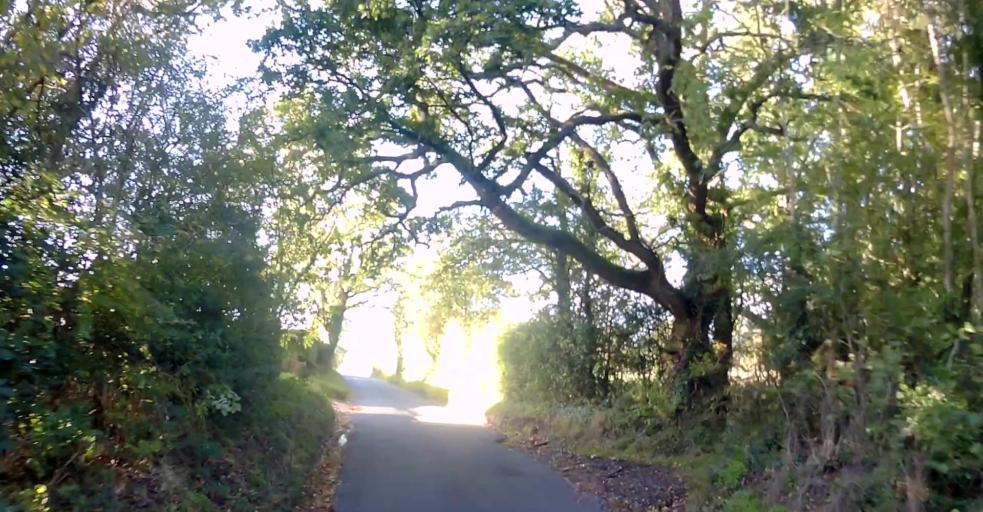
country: GB
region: England
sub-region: Hampshire
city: Long Sutton
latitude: 51.2121
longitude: -0.9084
